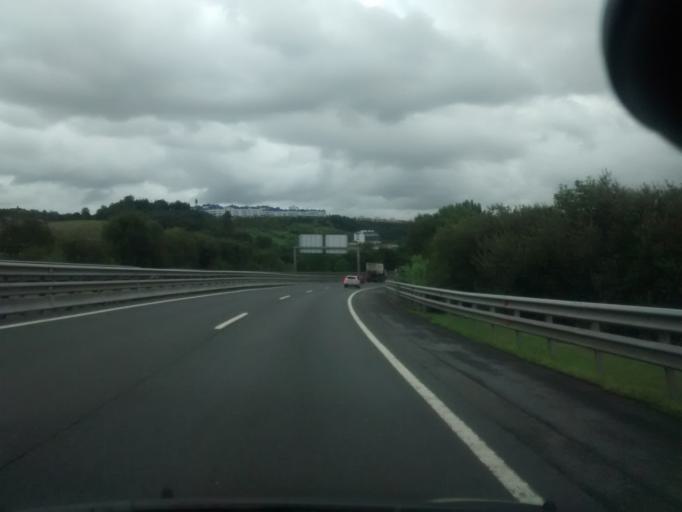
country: ES
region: Basque Country
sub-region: Provincia de Guipuzcoa
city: San Sebastian
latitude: 43.2989
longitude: -2.0059
